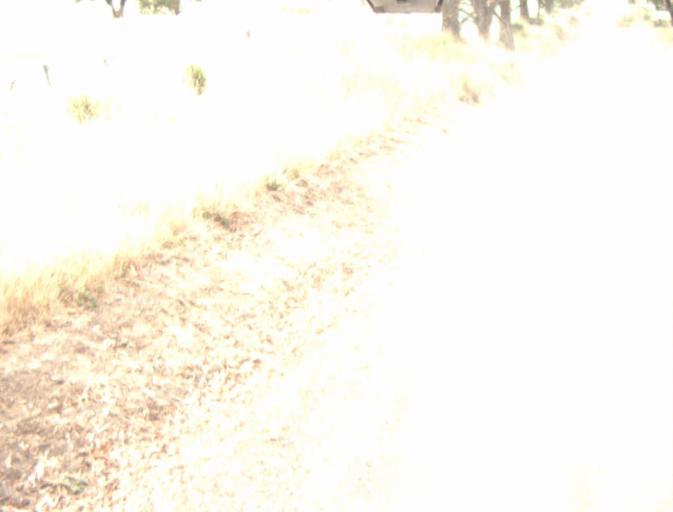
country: AU
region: Tasmania
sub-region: Dorset
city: Scottsdale
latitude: -41.4652
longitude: 147.5727
